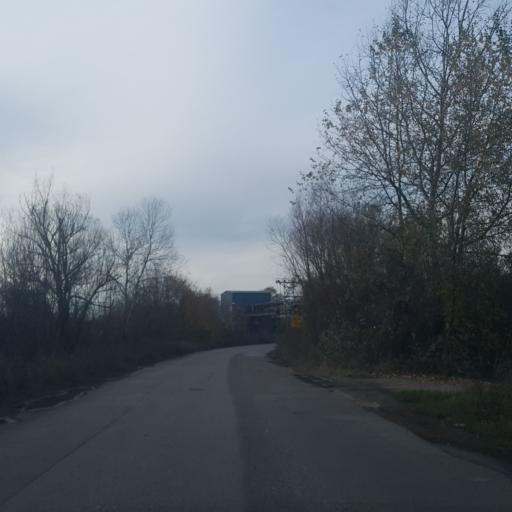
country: RS
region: Central Serbia
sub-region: Belgrade
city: Lazarevac
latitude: 44.4237
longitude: 20.2888
